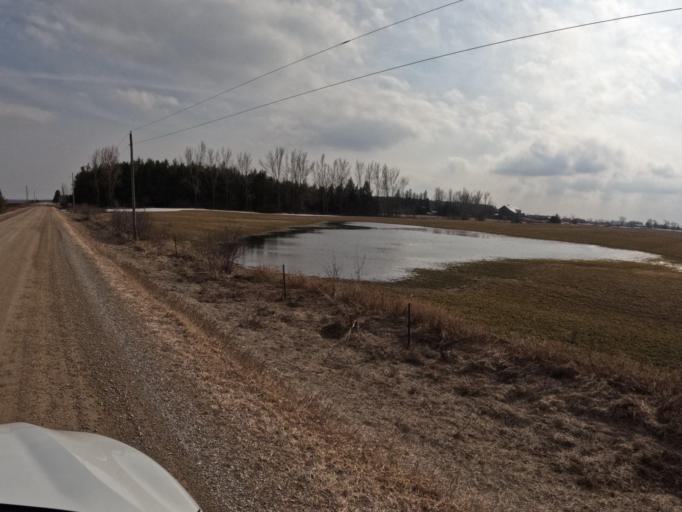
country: CA
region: Ontario
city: Shelburne
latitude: 43.9113
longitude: -80.2875
